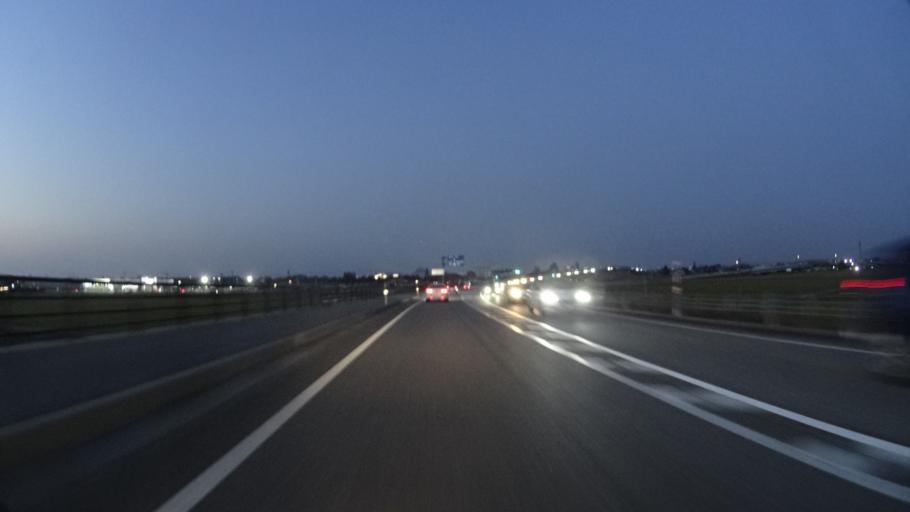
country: JP
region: Toyama
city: Uozu
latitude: 36.8748
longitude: 137.4275
